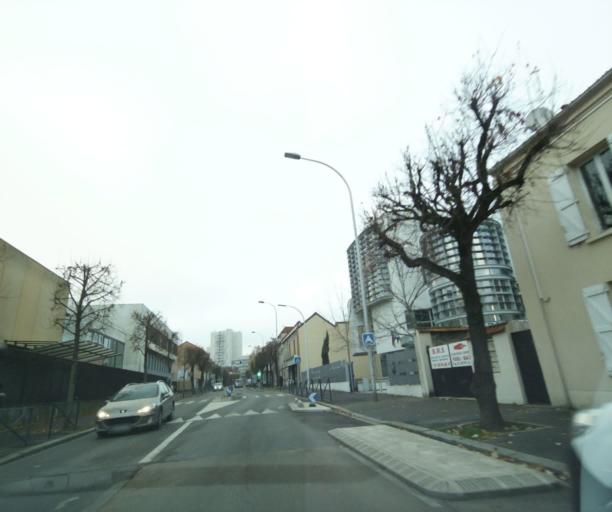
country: FR
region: Ile-de-France
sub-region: Departement de Seine-Saint-Denis
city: Villemomble
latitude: 48.8827
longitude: 2.5162
